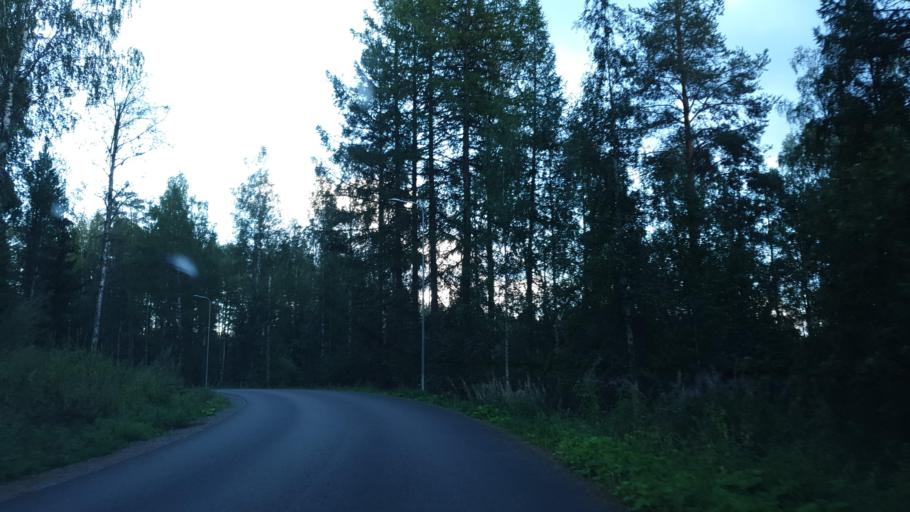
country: FI
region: Northern Savo
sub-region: Varkaus
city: Leppaevirta
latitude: 62.5830
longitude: 27.6142
